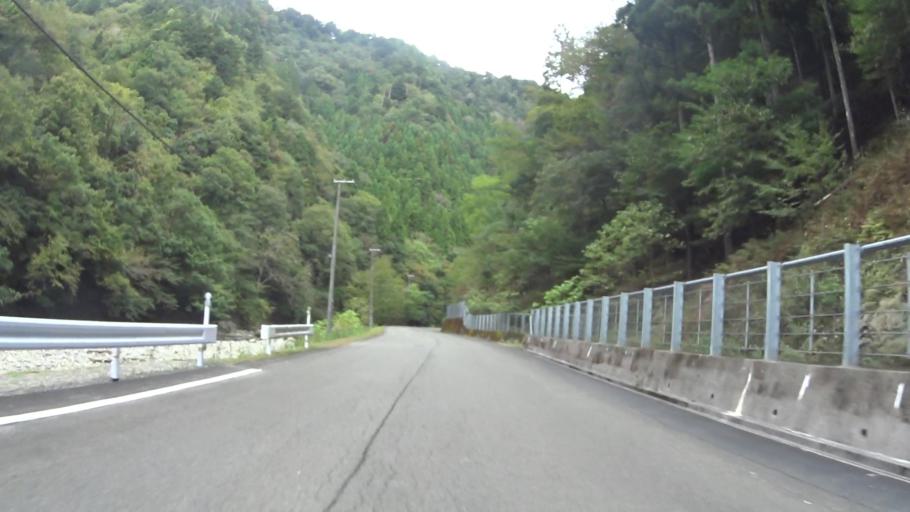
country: JP
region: Fukui
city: Obama
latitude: 35.2988
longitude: 135.6926
